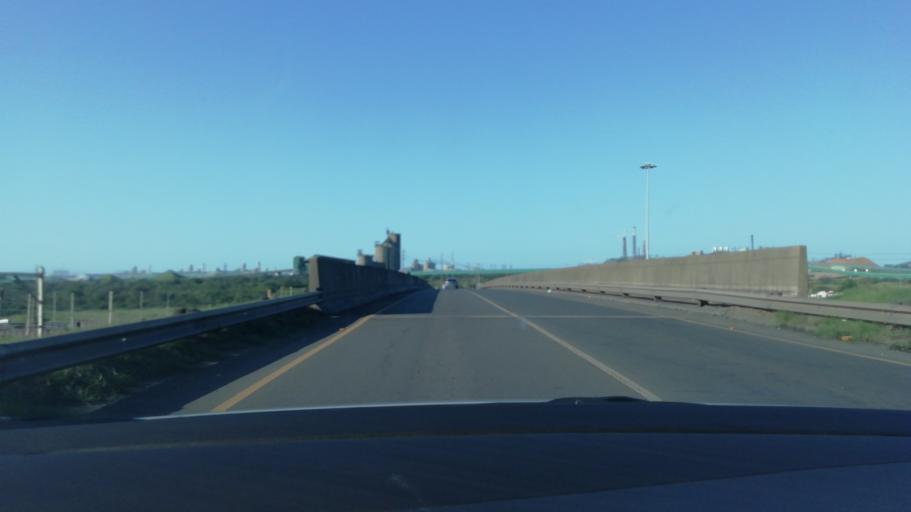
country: ZA
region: KwaZulu-Natal
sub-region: uThungulu District Municipality
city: Richards Bay
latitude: -28.7835
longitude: 32.0276
